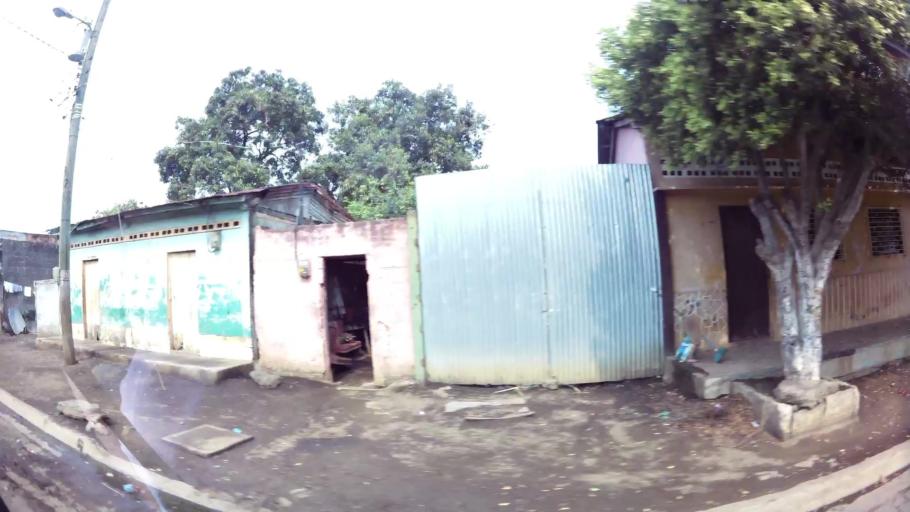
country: NI
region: Chinandega
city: Chinandega
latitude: 12.6351
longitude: -87.1403
